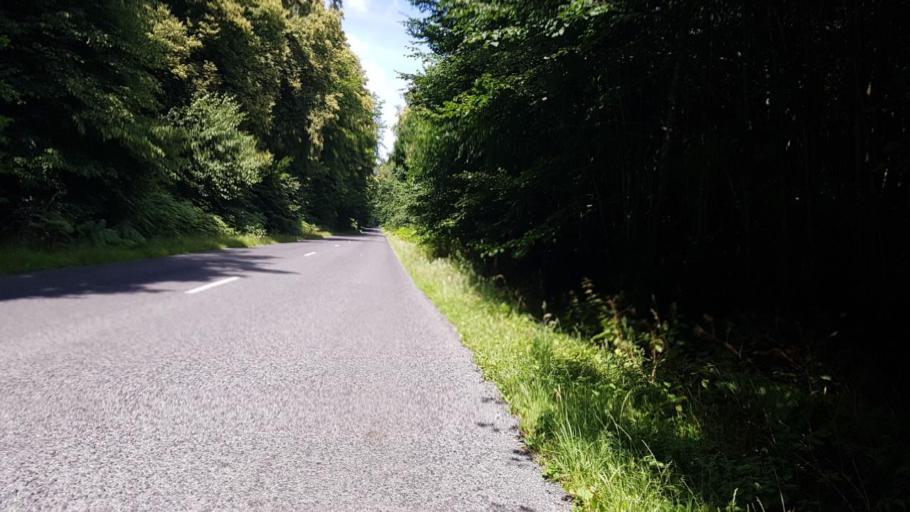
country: FR
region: Picardie
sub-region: Departement de l'Oise
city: Chiry-Ourscamp
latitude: 49.5417
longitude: 2.9857
